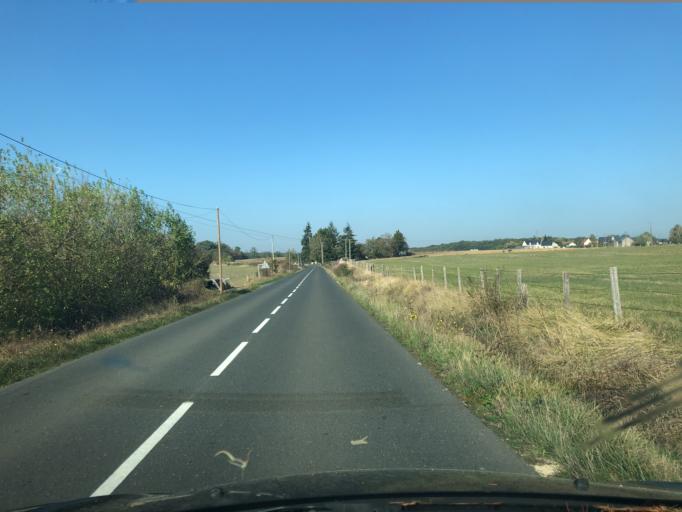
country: FR
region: Centre
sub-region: Departement d'Indre-et-Loire
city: Mettray
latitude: 47.4702
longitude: 0.6674
